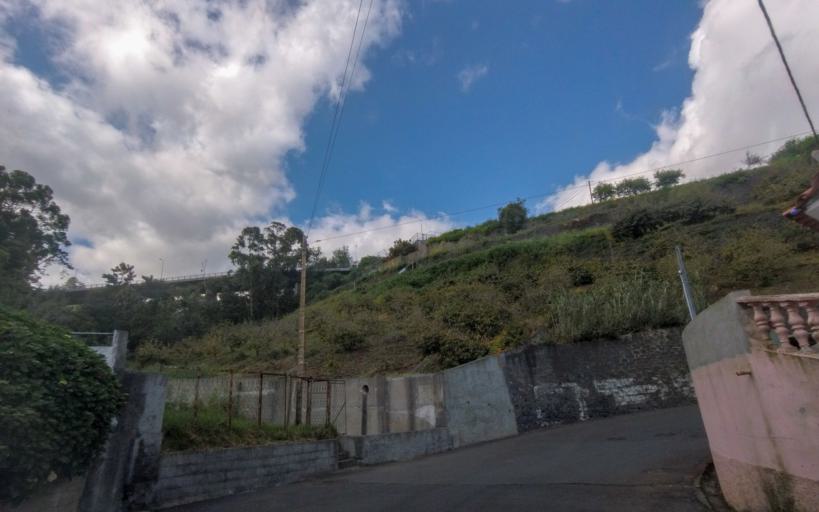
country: PT
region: Madeira
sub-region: Camara de Lobos
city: Curral das Freiras
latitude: 32.6776
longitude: -16.9482
